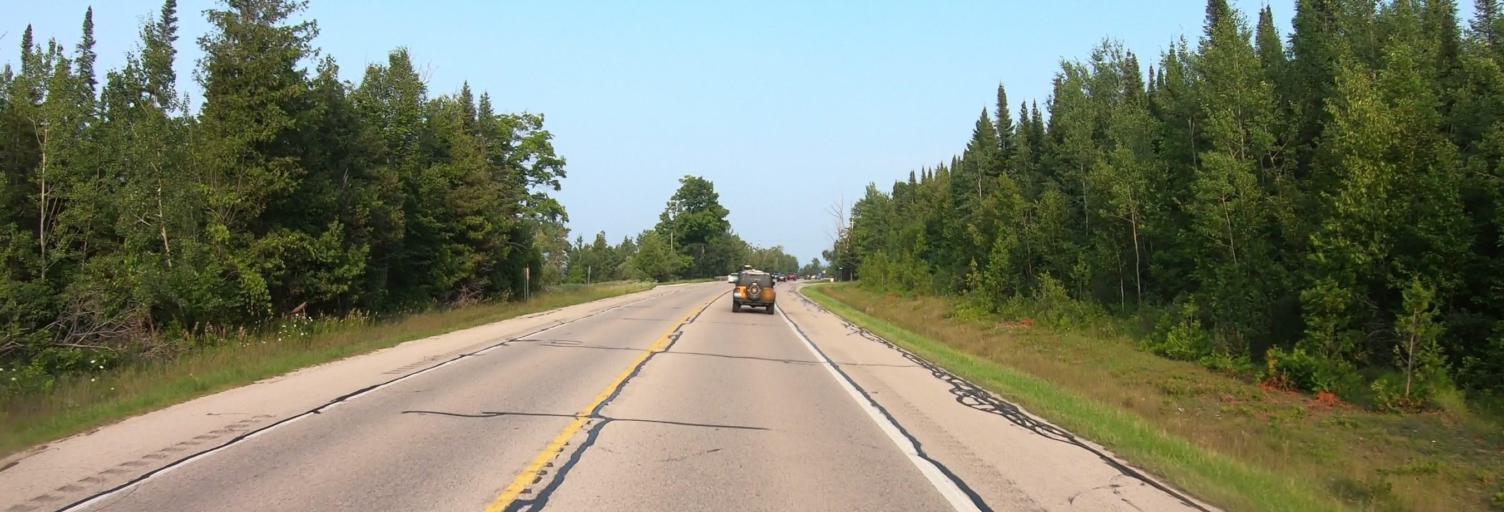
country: US
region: Michigan
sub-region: Charlevoix County
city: Charlevoix
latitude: 45.3692
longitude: -85.1344
